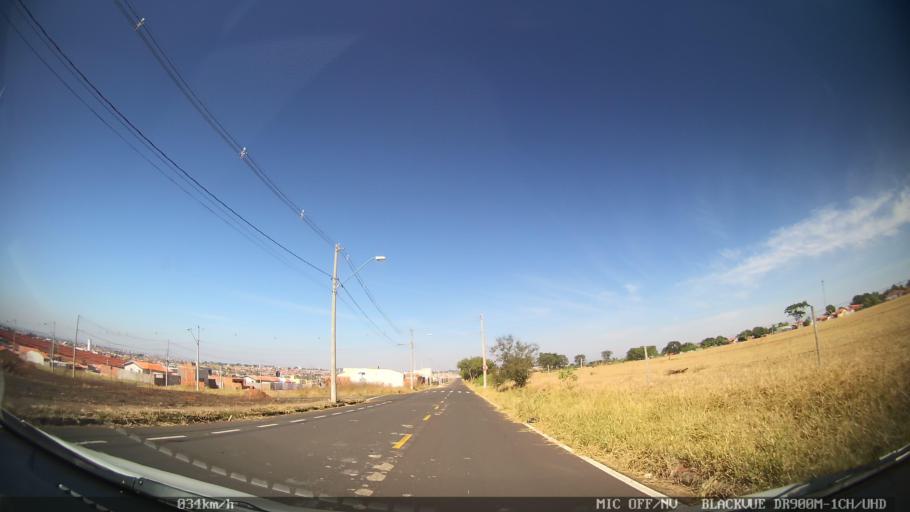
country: BR
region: Sao Paulo
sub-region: Sao Jose Do Rio Preto
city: Sao Jose do Rio Preto
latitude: -20.7511
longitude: -49.4253
